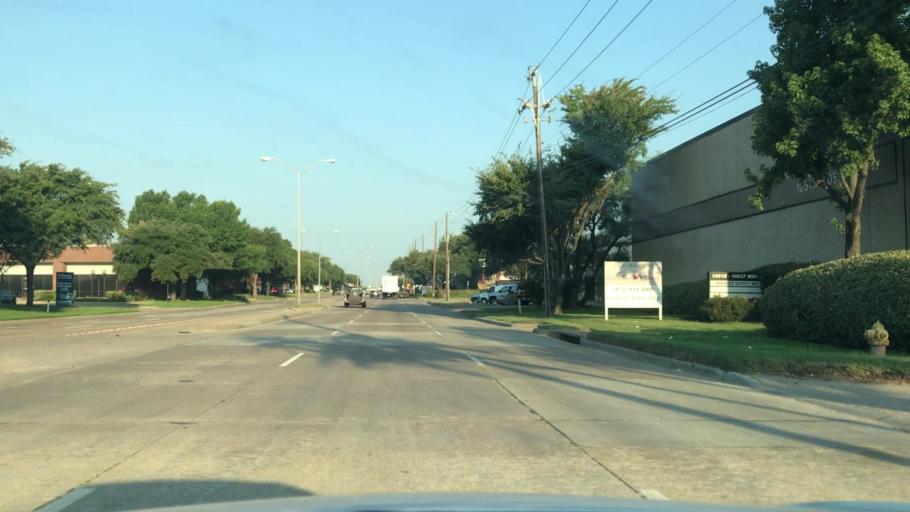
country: US
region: Texas
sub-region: Dallas County
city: Richardson
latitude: 32.8946
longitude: -96.7031
